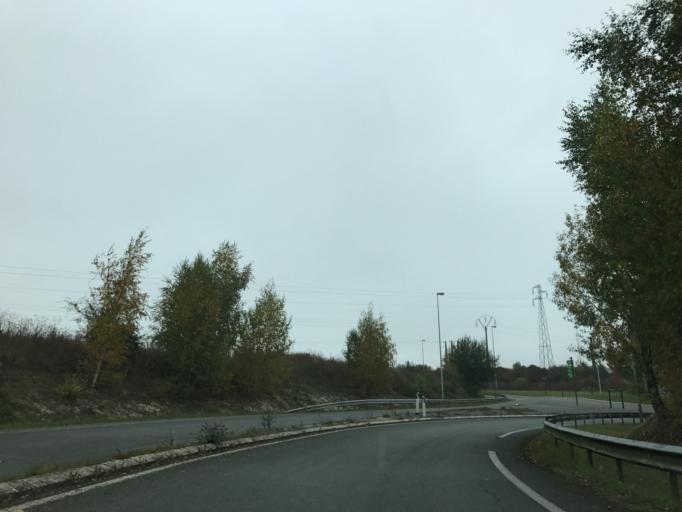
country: FR
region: Nord-Pas-de-Calais
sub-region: Departement du Pas-de-Calais
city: Saint-Laurent-Blangy
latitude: 50.3089
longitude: 2.8011
